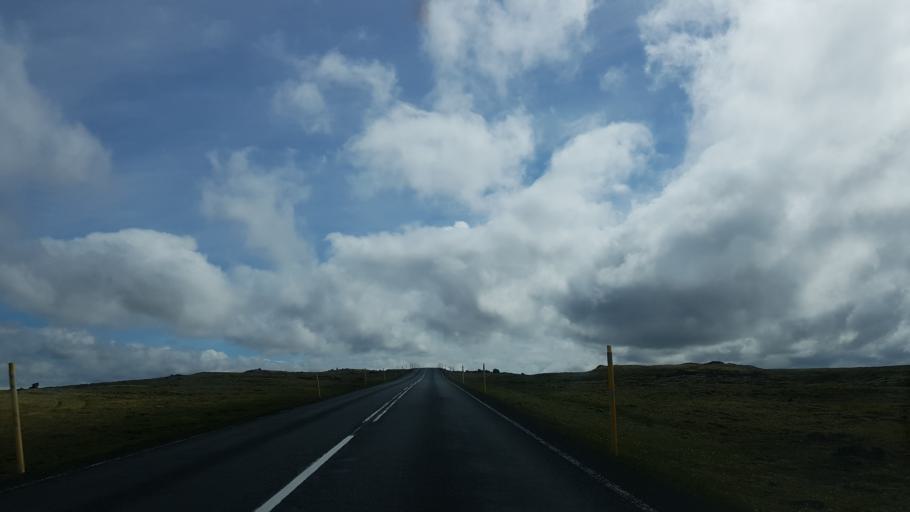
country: IS
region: West
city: Borgarnes
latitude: 64.9950
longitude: -21.0644
